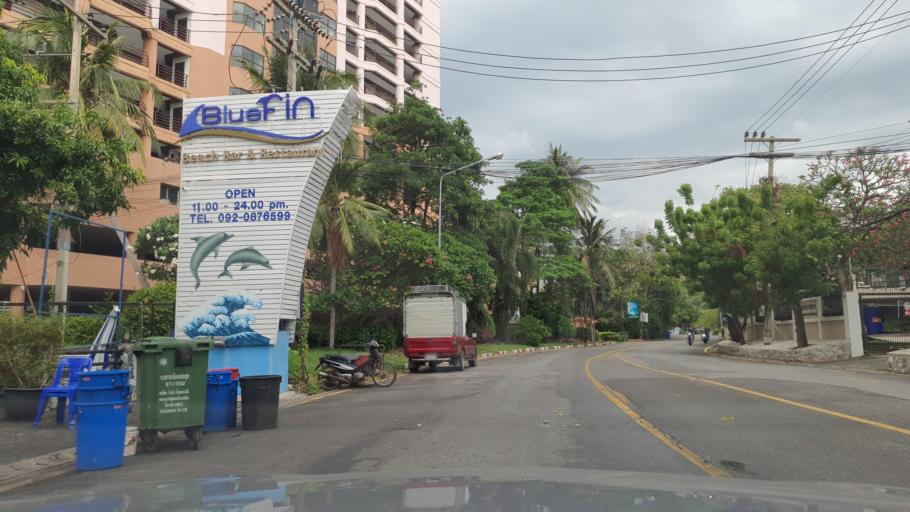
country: TH
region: Chon Buri
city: Chon Buri
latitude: 13.3093
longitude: 100.9031
